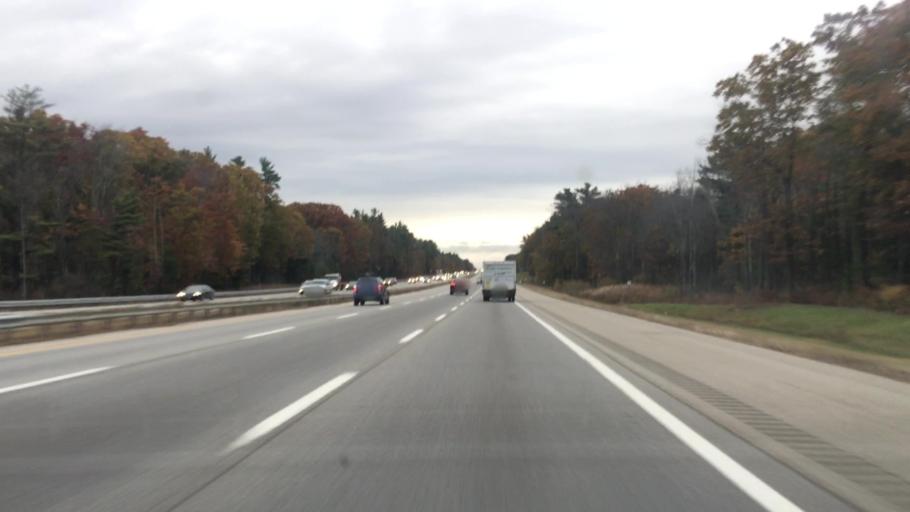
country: US
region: Maine
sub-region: Cumberland County
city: West Scarborough
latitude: 43.5564
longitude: -70.4224
